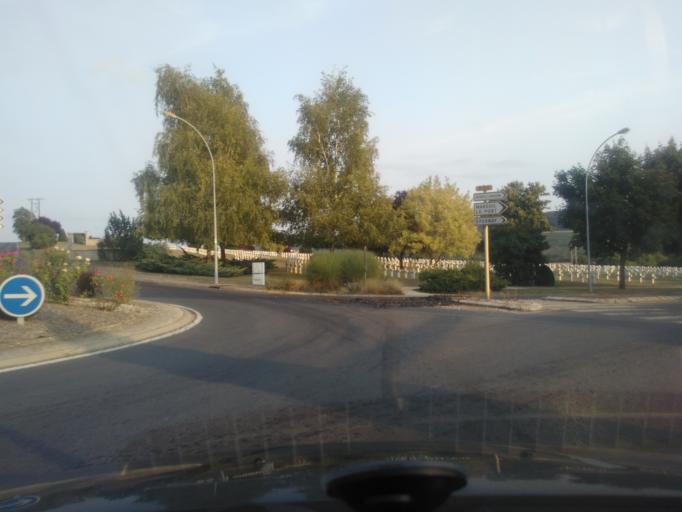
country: FR
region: Champagne-Ardenne
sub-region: Departement de la Marne
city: Chatillon-sur-Marne
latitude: 49.0911
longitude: 3.7643
